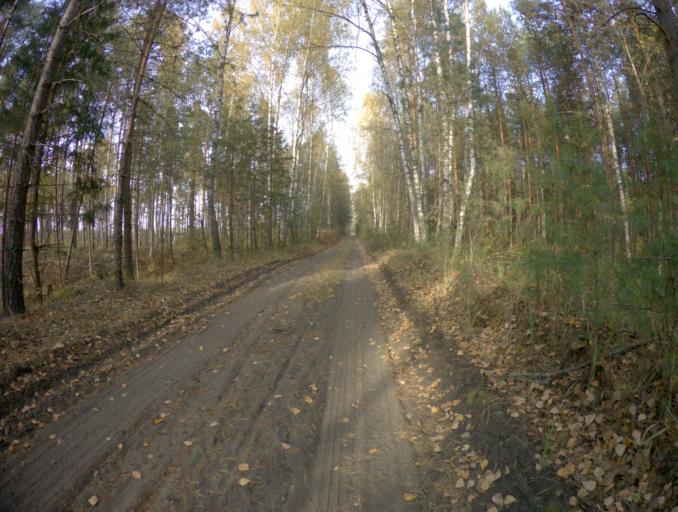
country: RU
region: Vladimir
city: Sobinka
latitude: 55.9538
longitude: 40.0594
